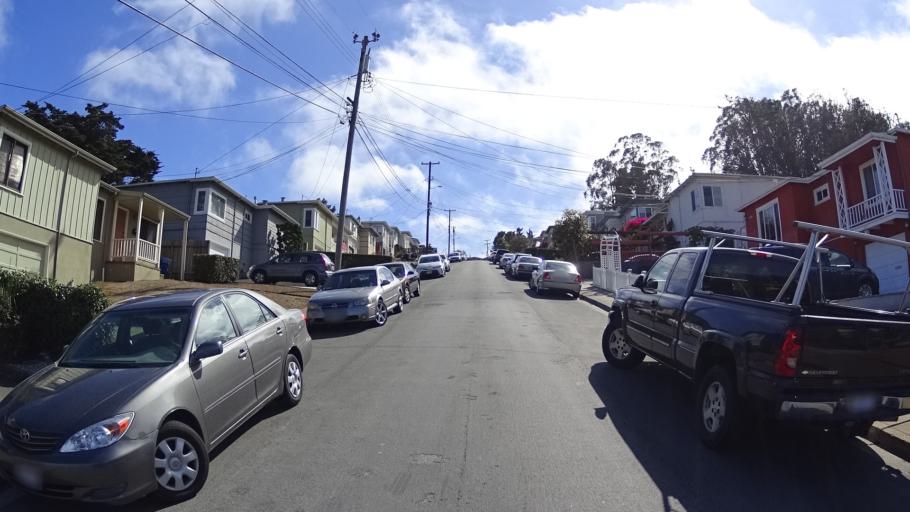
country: US
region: California
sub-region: San Mateo County
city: Broadmoor
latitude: 37.6884
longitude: -122.4800
